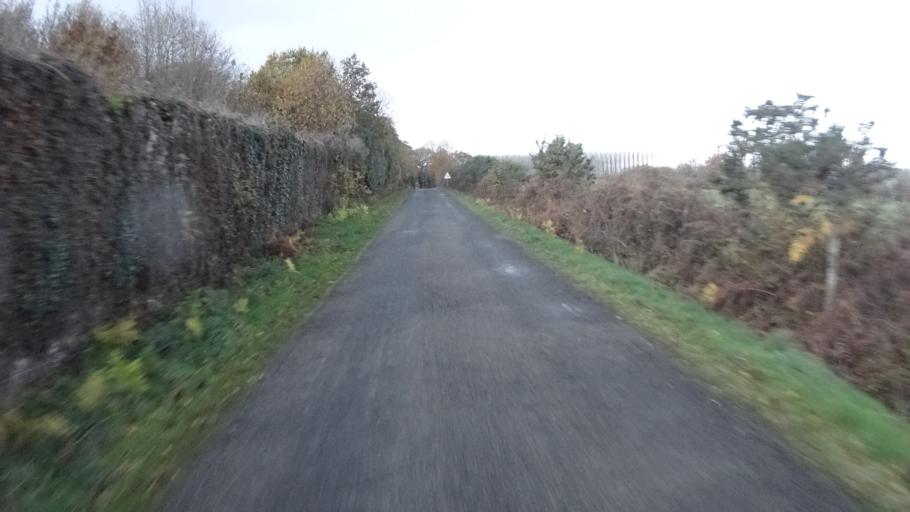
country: FR
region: Pays de la Loire
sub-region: Departement de la Loire-Atlantique
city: Avessac
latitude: 47.6658
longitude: -2.0037
